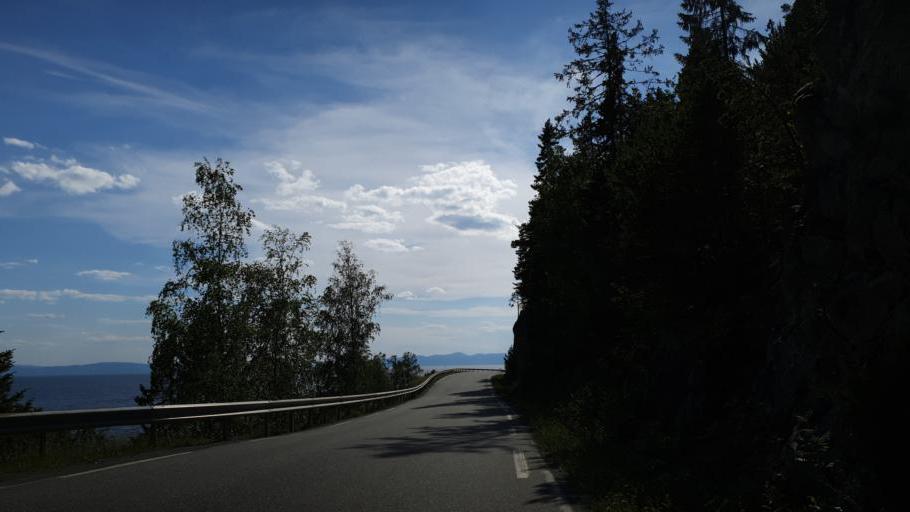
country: NO
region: Nord-Trondelag
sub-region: Leksvik
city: Leksvik
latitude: 63.6299
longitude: 10.5672
